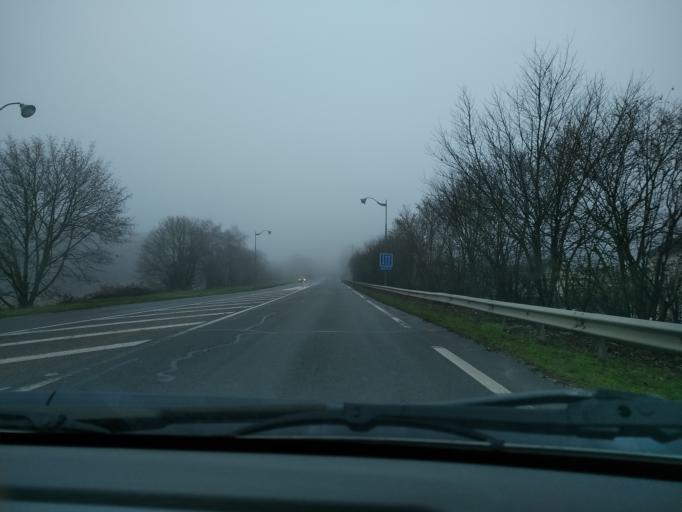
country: FR
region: Centre
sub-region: Departement d'Eure-et-Loir
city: Marboue
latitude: 48.1169
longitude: 1.3303
